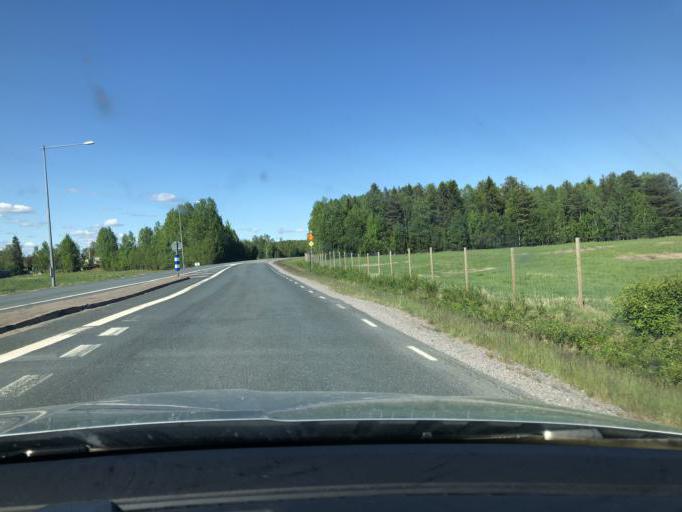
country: SE
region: Norrbotten
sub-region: Kalix Kommun
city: Kalix
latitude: 65.8420
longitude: 23.1943
